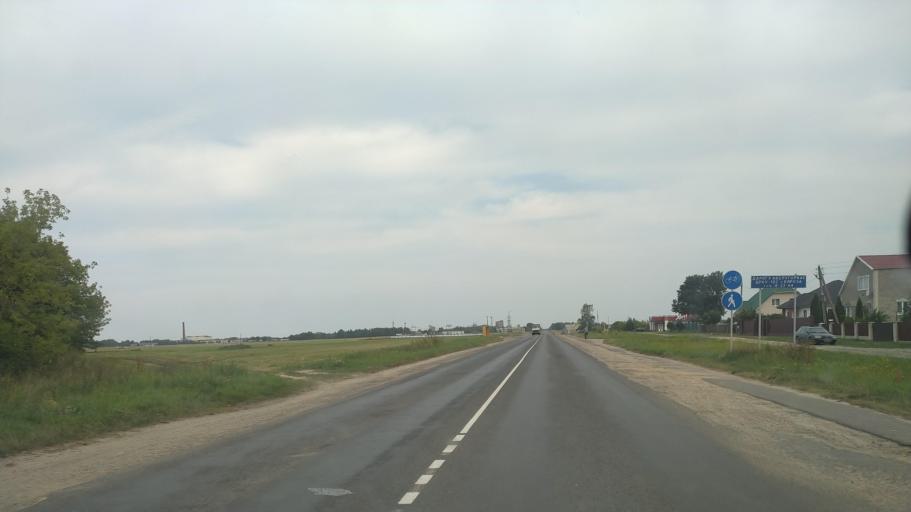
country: BY
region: Brest
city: Byaroza
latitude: 52.5455
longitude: 24.9593
